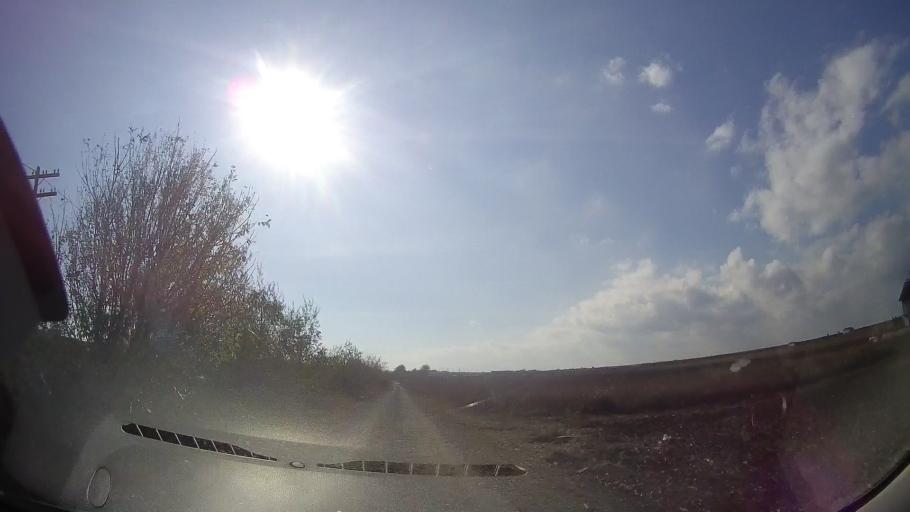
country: RO
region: Constanta
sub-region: Comuna Costinesti
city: Costinesti
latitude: 43.9668
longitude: 28.6405
